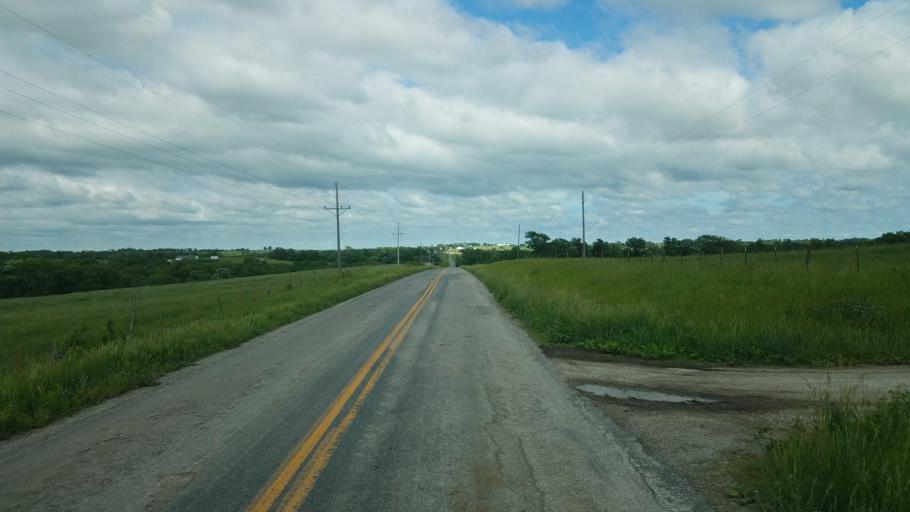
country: US
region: Missouri
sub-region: Mercer County
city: Princeton
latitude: 40.3002
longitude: -93.7177
